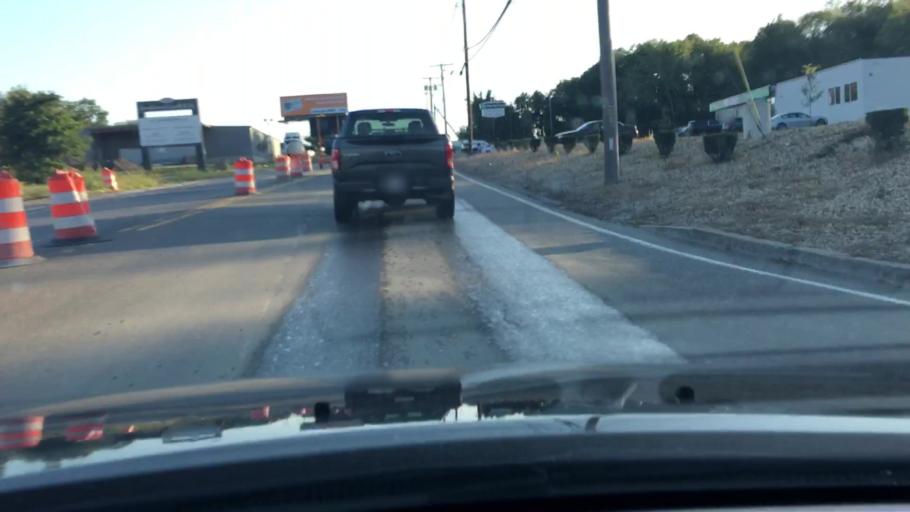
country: US
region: Massachusetts
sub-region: Worcester County
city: Sunderland
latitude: 42.2342
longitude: -71.7501
